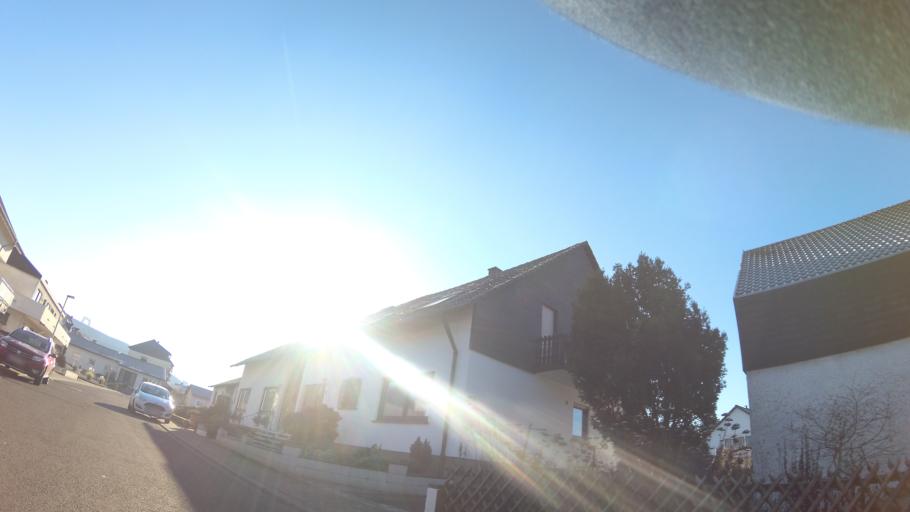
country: DE
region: Saarland
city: Saarlouis
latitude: 49.3273
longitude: 6.7744
